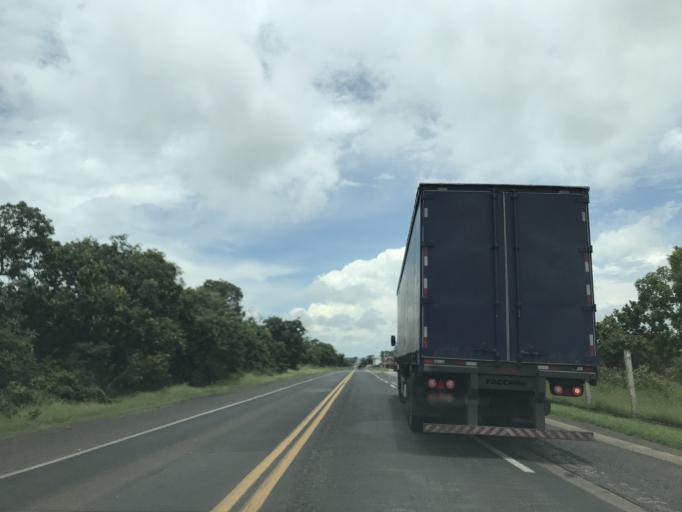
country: BR
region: Minas Gerais
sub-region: Frutal
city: Frutal
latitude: -19.7611
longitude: -48.9665
